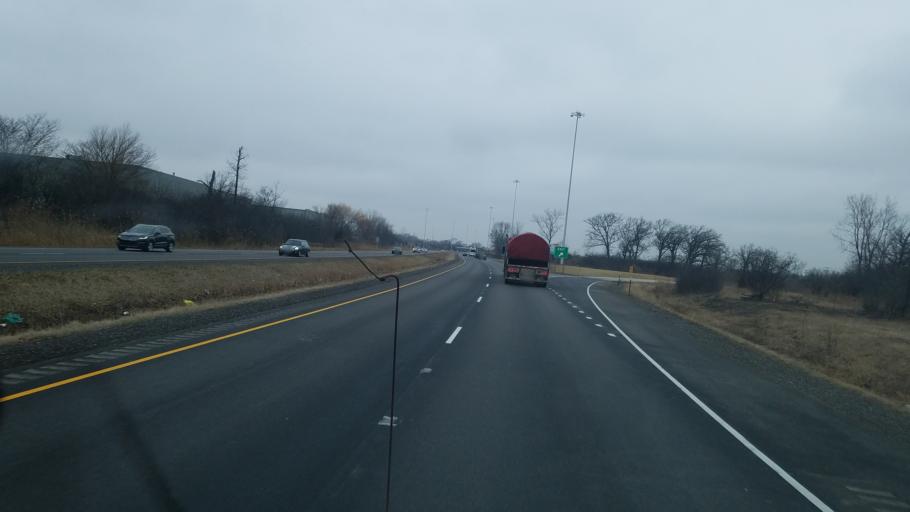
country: US
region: Illinois
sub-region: Lake County
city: Park City
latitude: 42.3412
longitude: -87.8873
